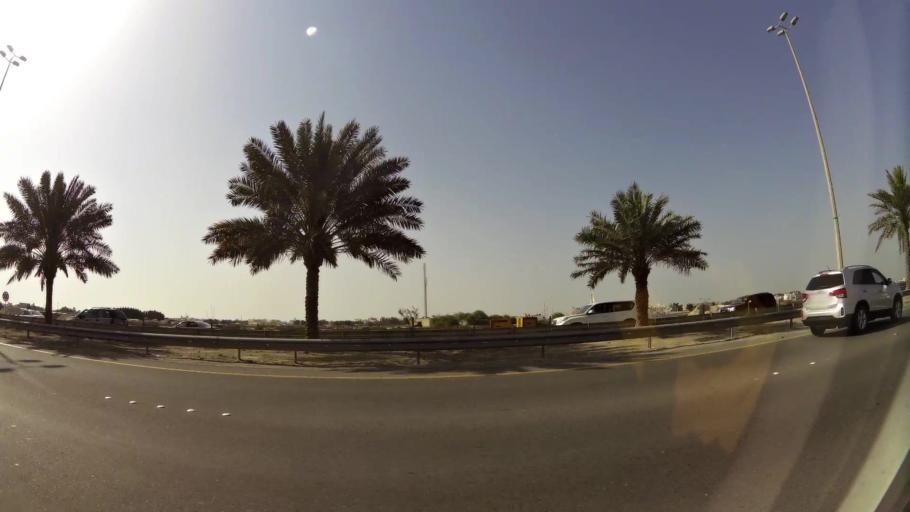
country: BH
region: Manama
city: Jidd Hafs
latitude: 26.2026
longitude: 50.5127
